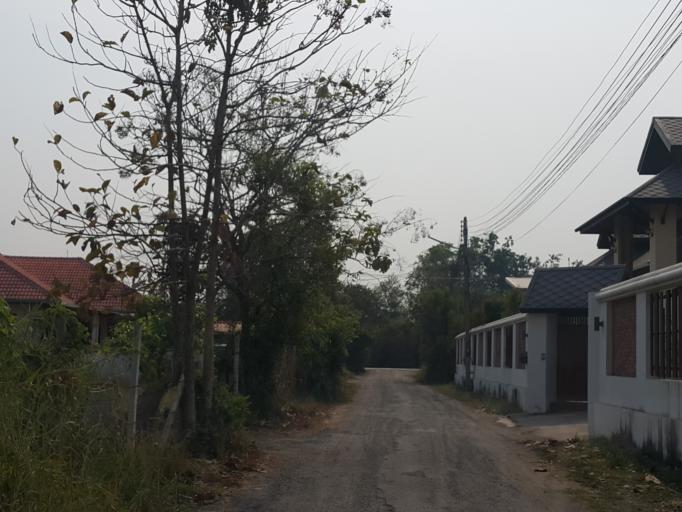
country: TH
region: Chiang Mai
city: San Kamphaeng
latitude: 18.7485
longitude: 99.0763
